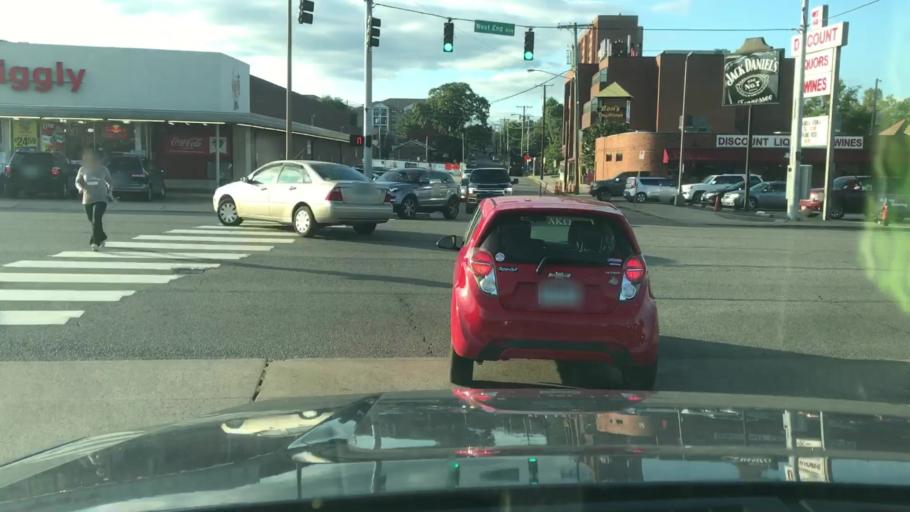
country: US
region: Tennessee
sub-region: Davidson County
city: Nashville
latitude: 36.1440
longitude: -86.8131
